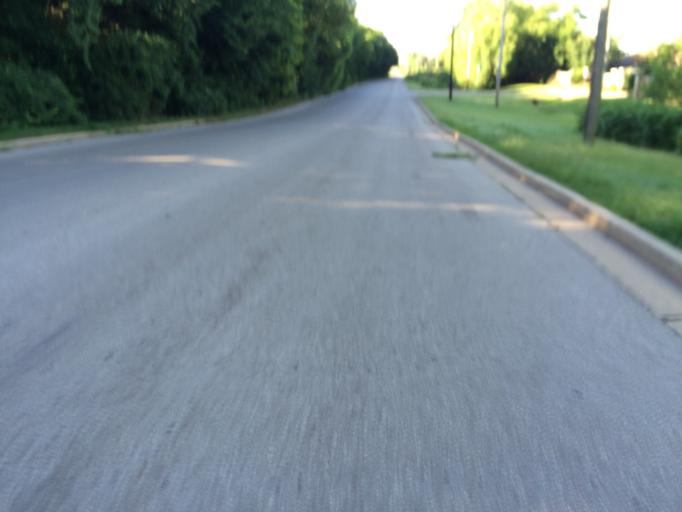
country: US
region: Oklahoma
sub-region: Cleveland County
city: Norman
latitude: 35.1801
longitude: -97.4502
